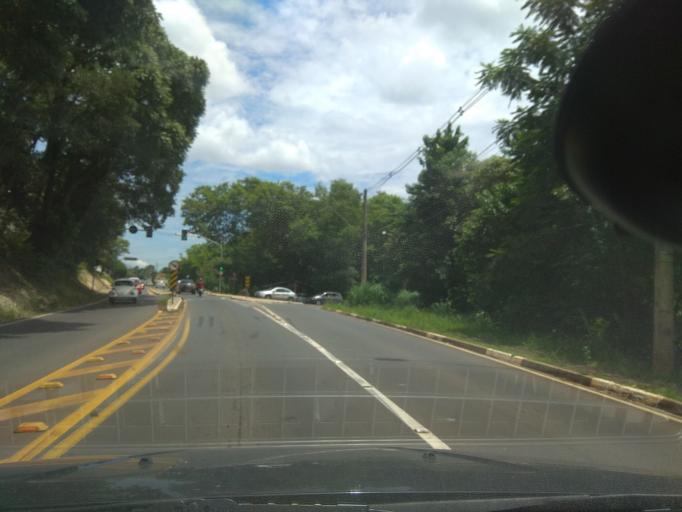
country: BR
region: Sao Paulo
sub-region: Paulinia
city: Paulinia
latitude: -22.8025
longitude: -47.0773
